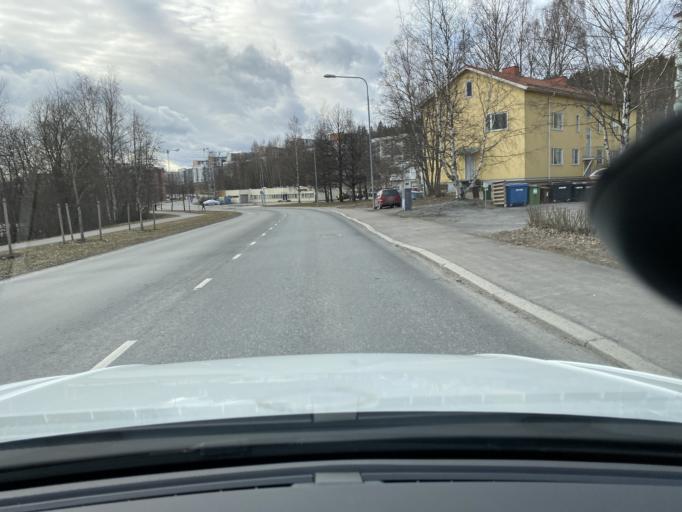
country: FI
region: Pirkanmaa
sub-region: Tampere
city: Tampere
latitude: 61.4902
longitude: 23.7967
